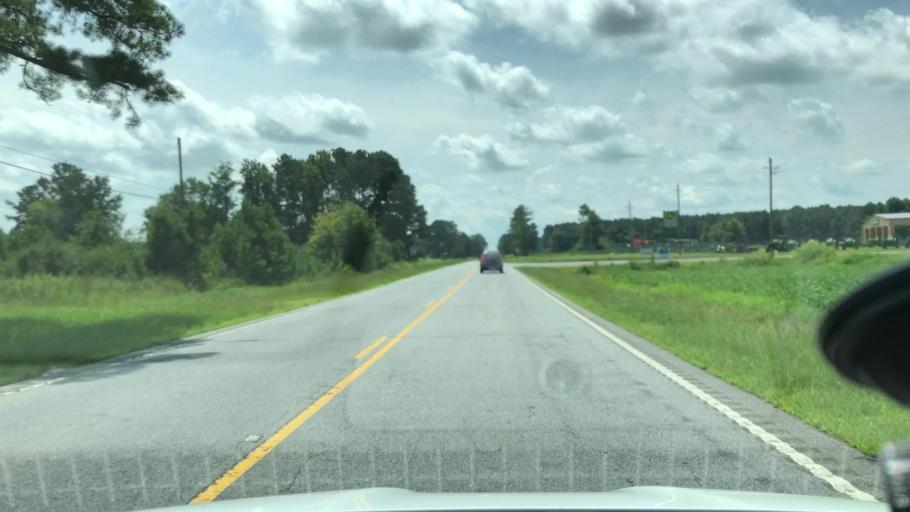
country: US
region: North Carolina
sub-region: Beaufort County
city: Washington
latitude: 35.6525
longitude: -77.0707
